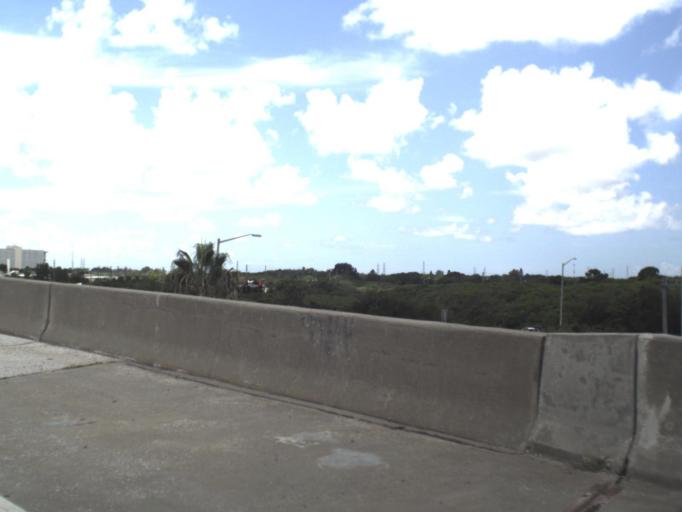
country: US
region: Florida
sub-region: Pinellas County
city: South Highpoint
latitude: 27.9114
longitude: -82.7009
